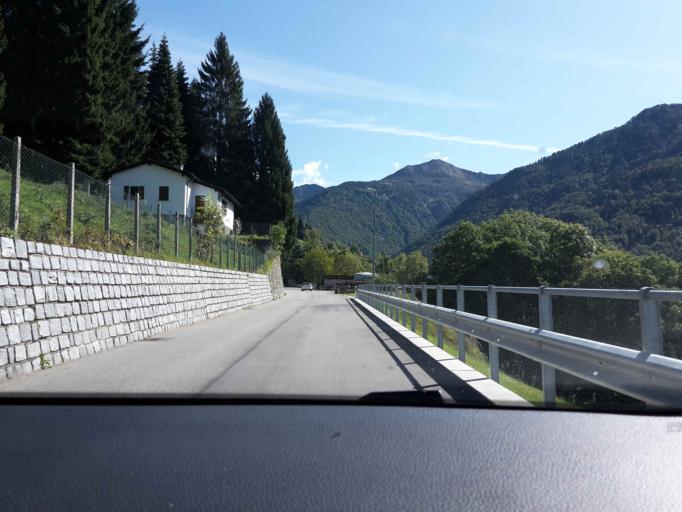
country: CH
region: Ticino
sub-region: Bellinzona District
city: Lumino
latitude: 46.1710
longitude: 9.0775
